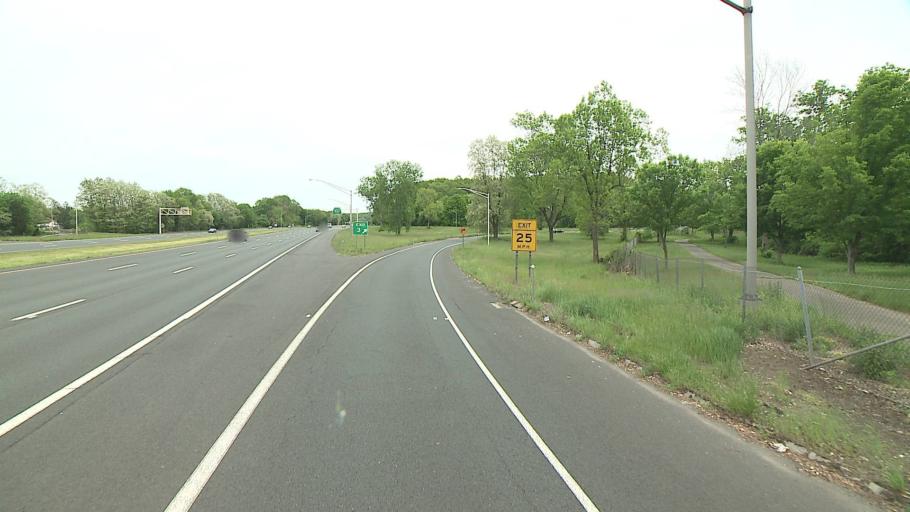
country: US
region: Connecticut
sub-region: Hartford County
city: Manchester
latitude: 41.7624
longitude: -72.5205
